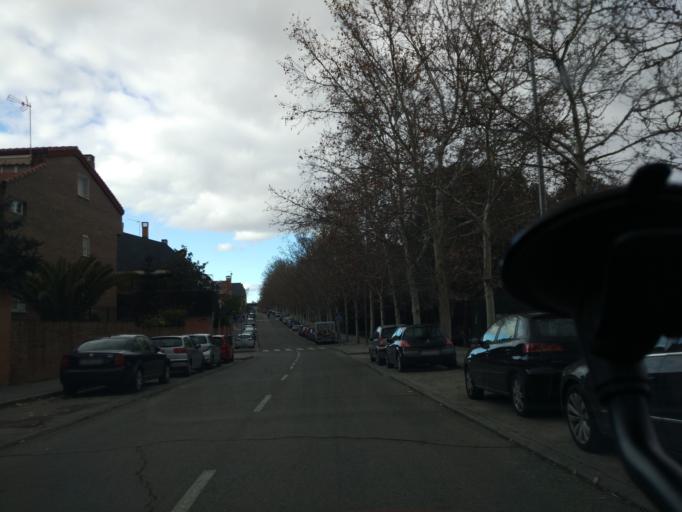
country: ES
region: Madrid
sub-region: Provincia de Madrid
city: San Blas
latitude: 40.4418
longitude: -3.6297
